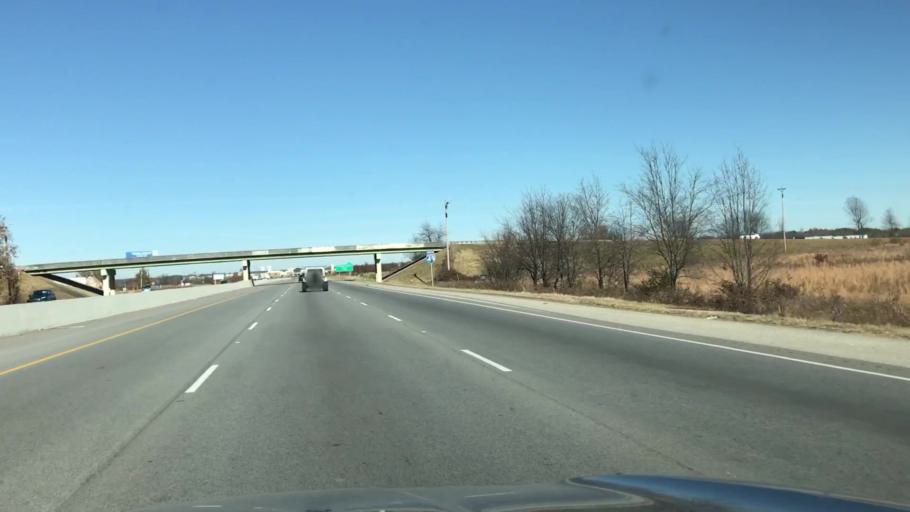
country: US
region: Arkansas
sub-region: Benton County
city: Lowell
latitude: 36.2640
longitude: -94.1502
